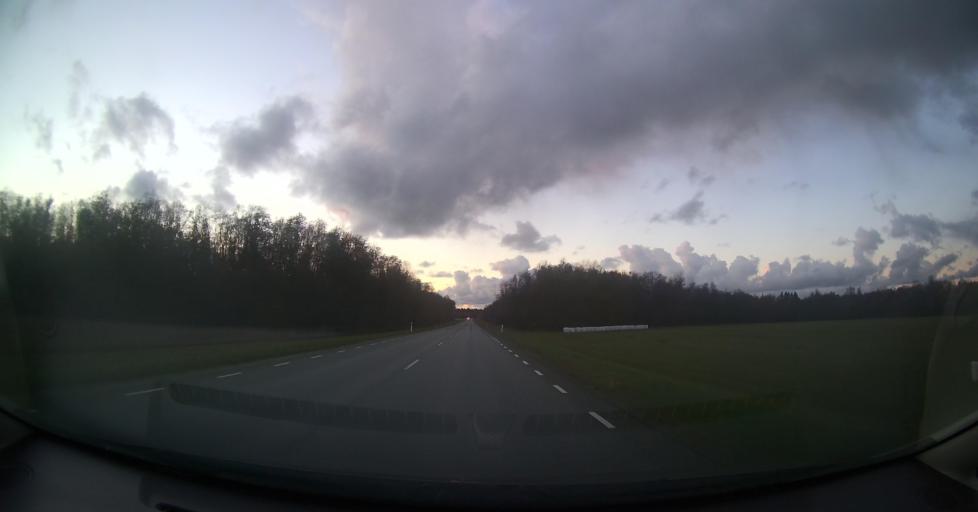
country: EE
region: Harju
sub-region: Raasiku vald
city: Raasiku
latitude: 59.4134
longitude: 25.2318
